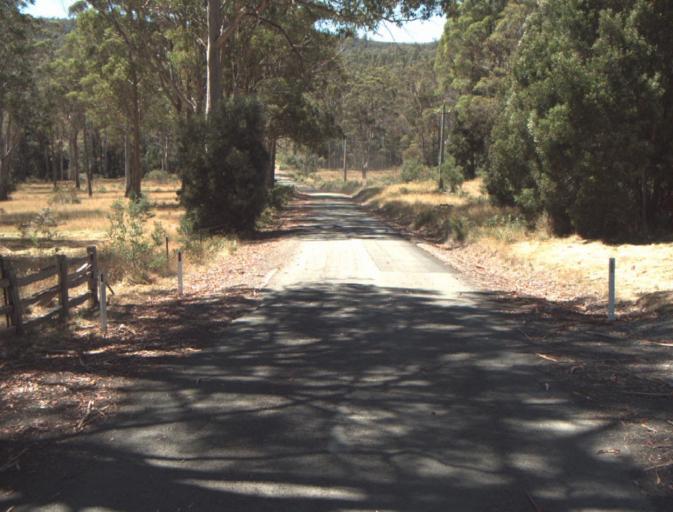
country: AU
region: Tasmania
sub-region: Launceston
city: Newstead
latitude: -41.3433
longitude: 147.3619
